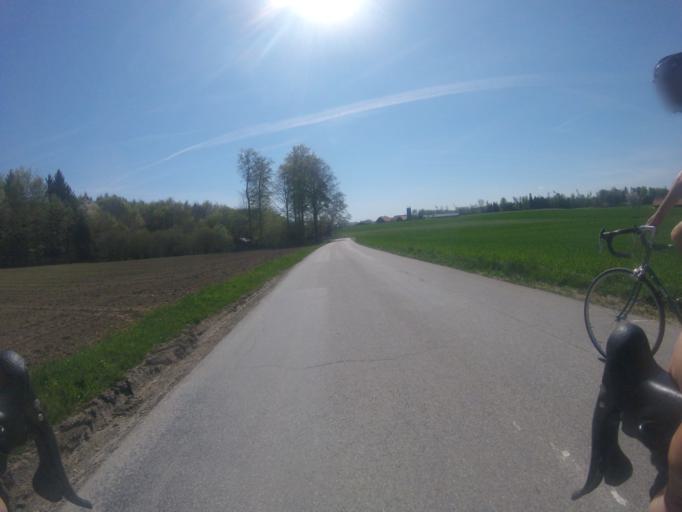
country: CH
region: Fribourg
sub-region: Sense District
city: Flamatt
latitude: 46.9171
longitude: 7.3473
